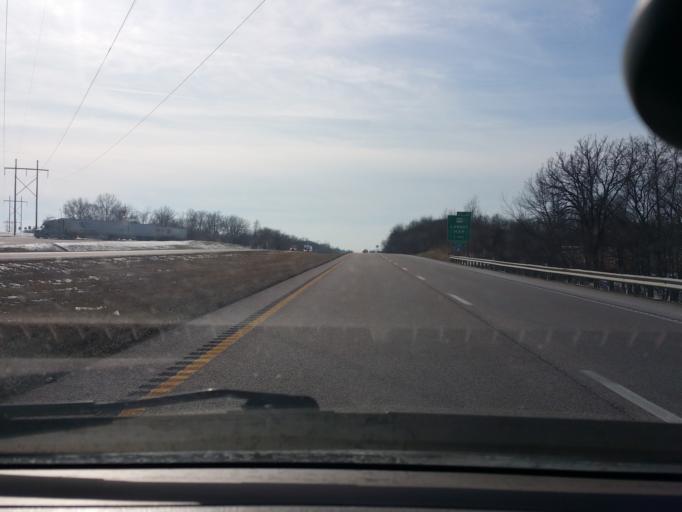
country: US
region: Missouri
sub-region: Clinton County
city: Lathrop
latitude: 39.4766
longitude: -94.3105
